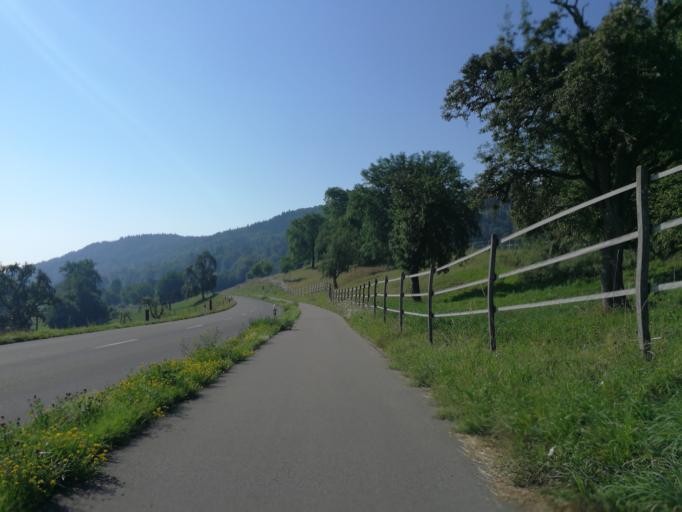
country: DE
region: Baden-Wuerttemberg
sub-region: Freiburg Region
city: Gailingen
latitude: 47.6811
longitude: 8.7700
